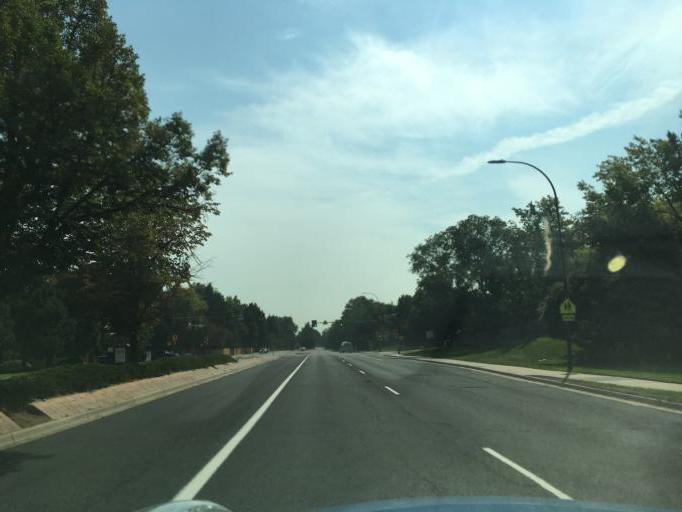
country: US
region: Colorado
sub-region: Jefferson County
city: Arvada
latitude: 39.8418
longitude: -105.1008
